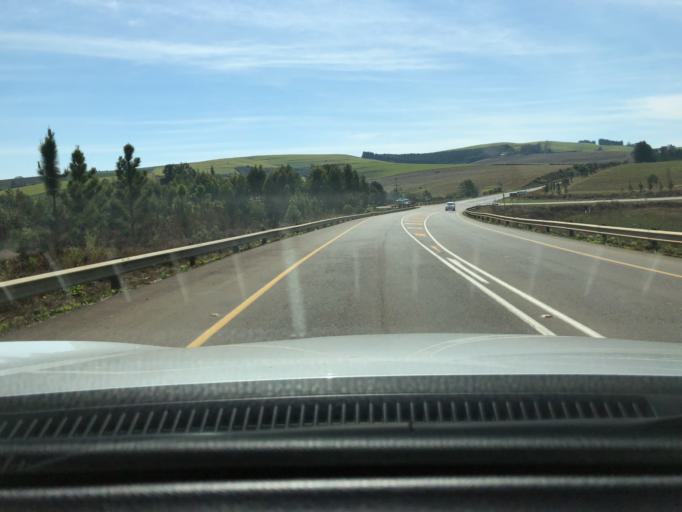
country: ZA
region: KwaZulu-Natal
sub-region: uMgungundlovu District Municipality
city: Richmond
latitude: -29.8736
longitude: 30.2839
